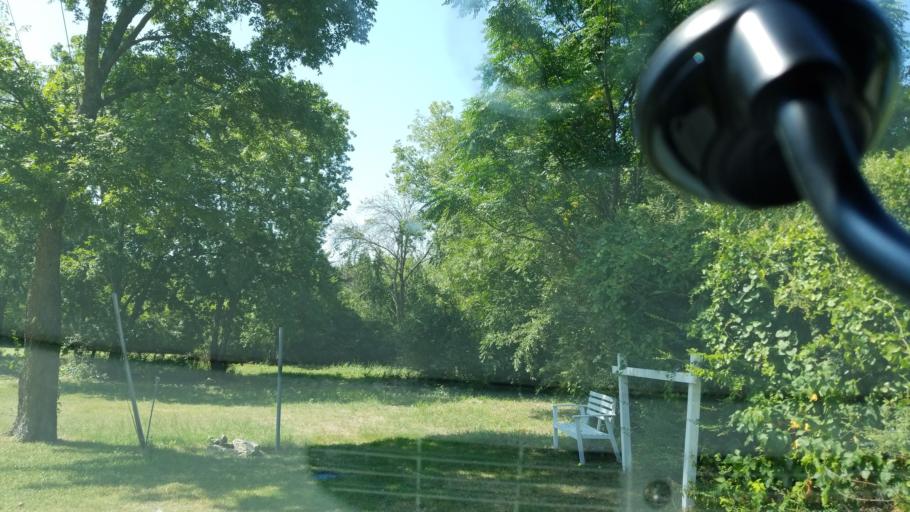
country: US
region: Texas
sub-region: Dallas County
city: Cockrell Hill
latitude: 32.7136
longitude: -96.8805
